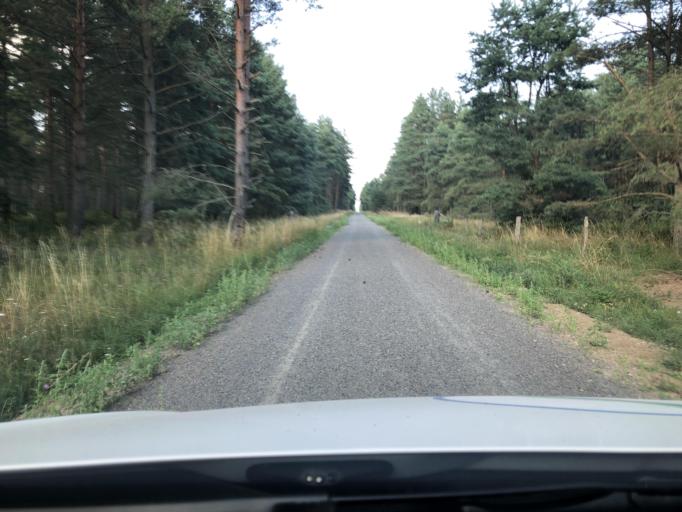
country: SE
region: Skane
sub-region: Kristianstads Kommun
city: Norra Asum
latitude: 55.9239
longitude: 14.1262
